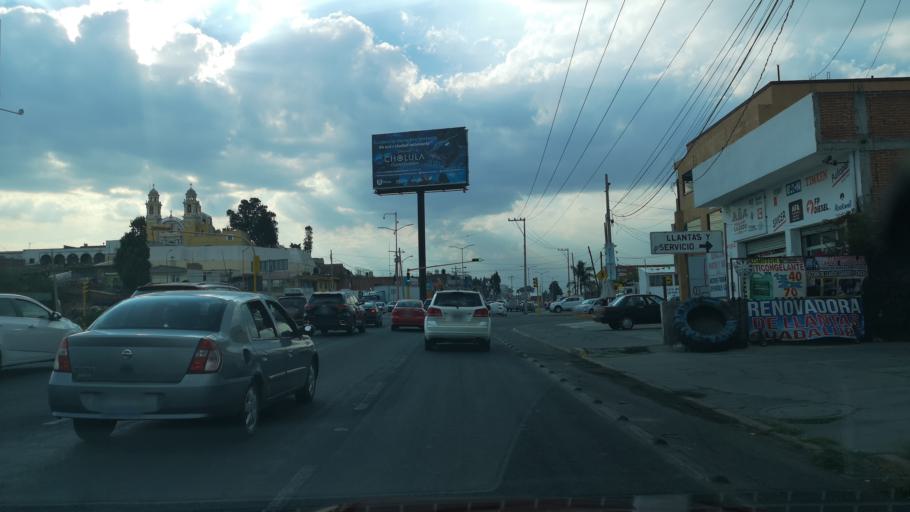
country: MX
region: Puebla
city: Cholula
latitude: 19.0715
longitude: -98.3150
